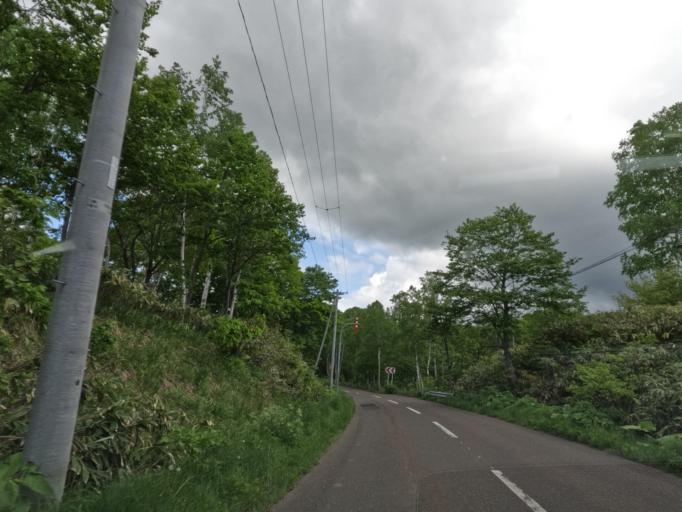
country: JP
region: Hokkaido
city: Tobetsu
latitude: 43.4643
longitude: 141.5993
